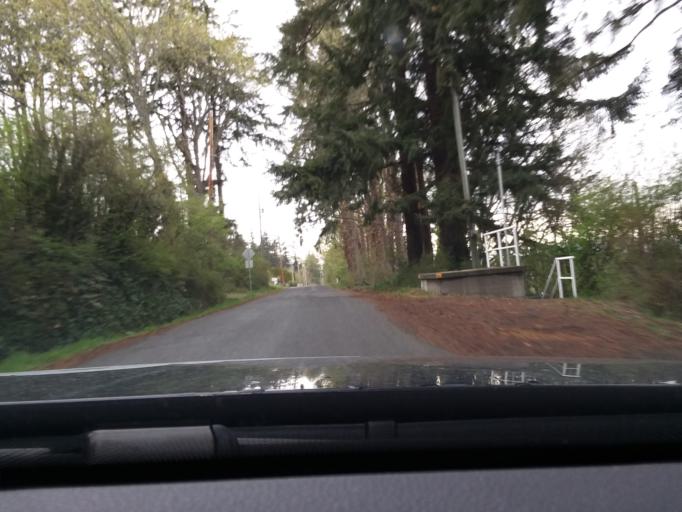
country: CA
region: British Columbia
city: North Saanich
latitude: 48.5509
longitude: -123.3900
